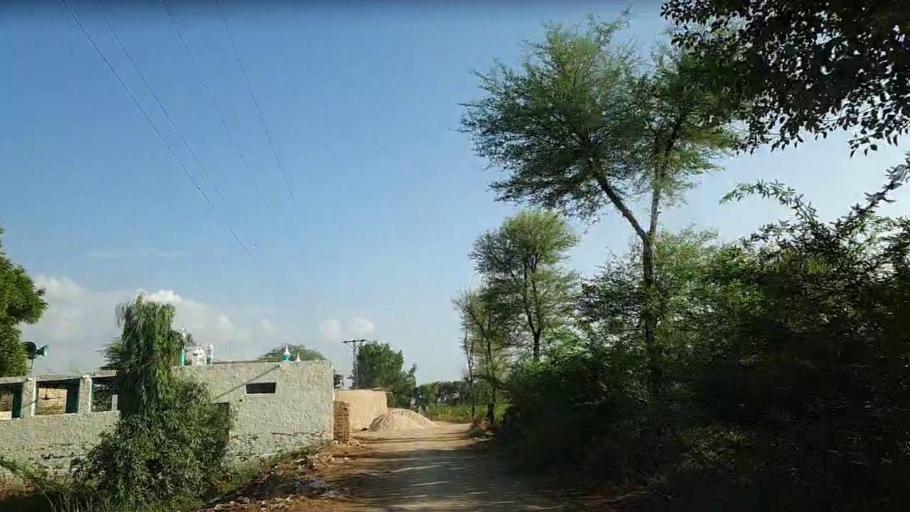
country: PK
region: Sindh
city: Hingorja
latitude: 27.0922
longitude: 68.3648
